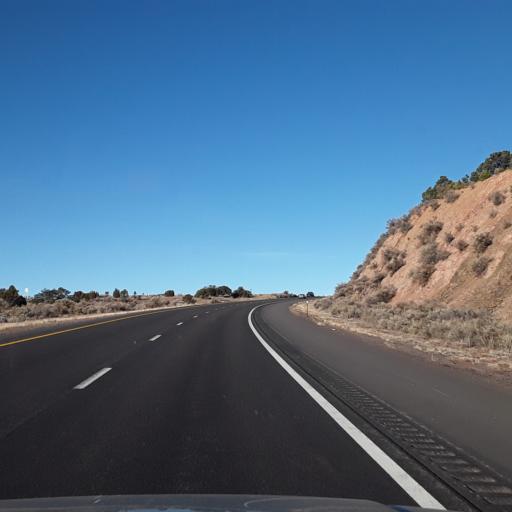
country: US
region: New Mexico
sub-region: Santa Fe County
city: Eldorado at Santa Fe
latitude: 35.5375
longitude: -105.8541
